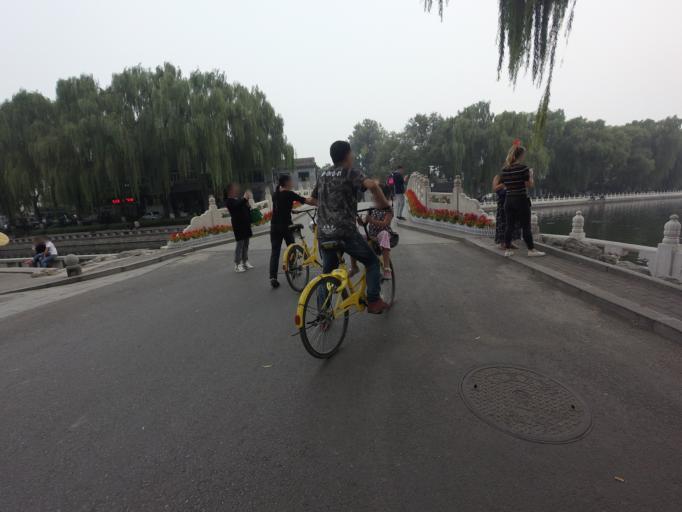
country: CN
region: Beijing
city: Jingshan
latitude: 39.9352
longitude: 116.3890
